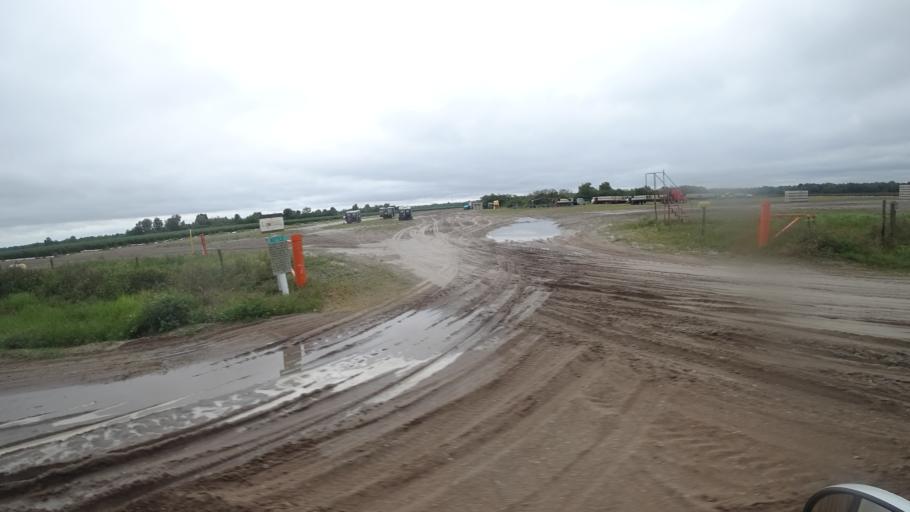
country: US
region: Florida
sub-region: Hillsborough County
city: Wimauma
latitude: 27.5924
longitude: -82.3109
